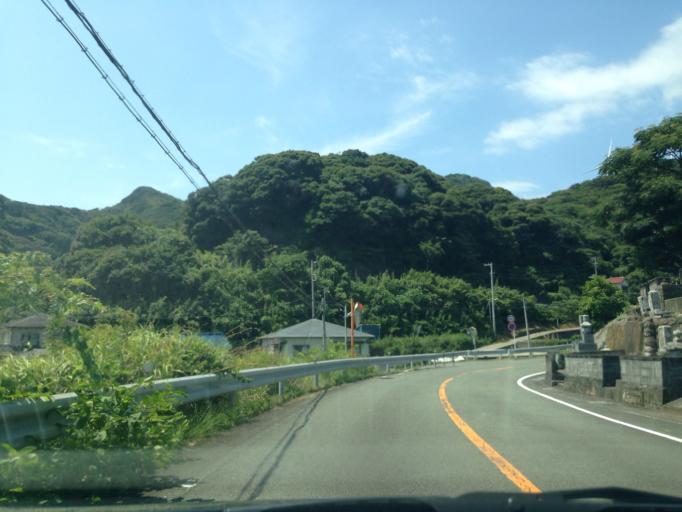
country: JP
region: Shizuoka
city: Shimoda
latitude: 34.6118
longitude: 138.8414
